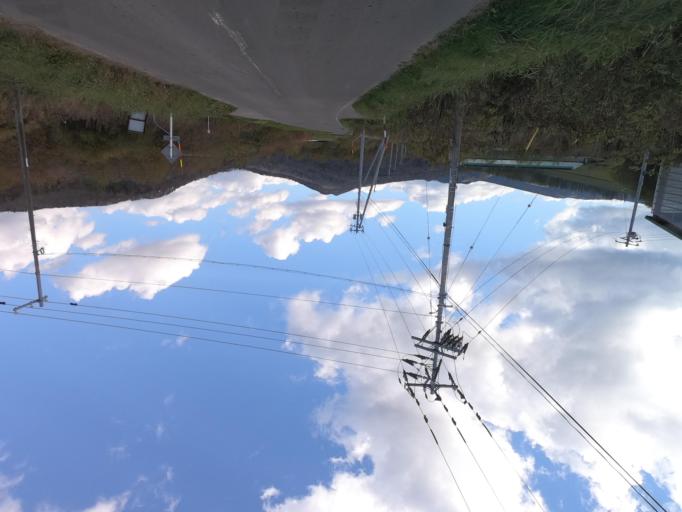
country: JP
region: Hokkaido
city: Otofuke
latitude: 43.2885
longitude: 143.2308
